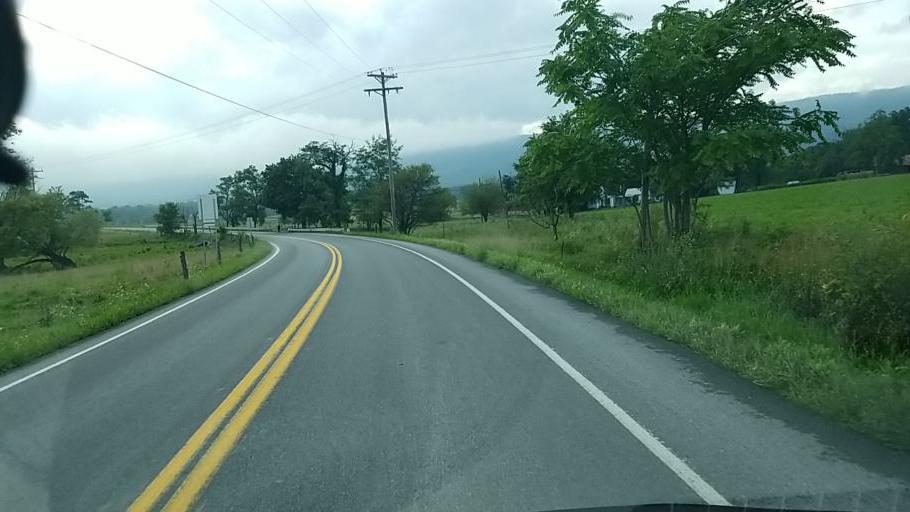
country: US
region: Pennsylvania
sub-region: Cumberland County
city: Shippensburg
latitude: 40.1583
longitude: -77.5859
